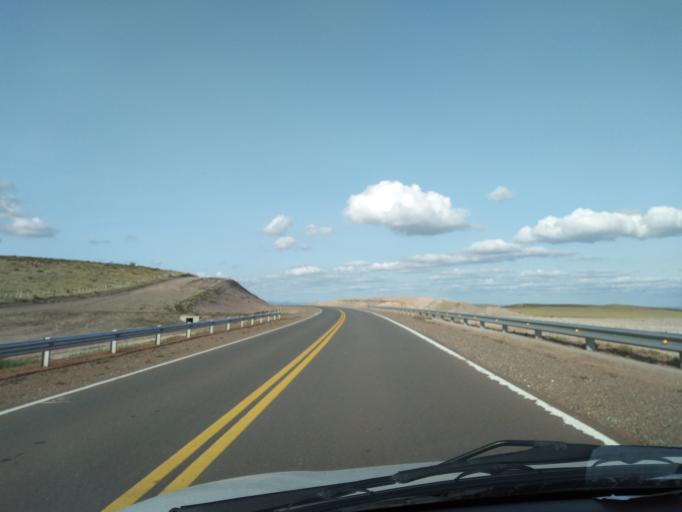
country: AR
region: Mendoza
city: Malargue
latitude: -34.8205
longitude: -69.2520
